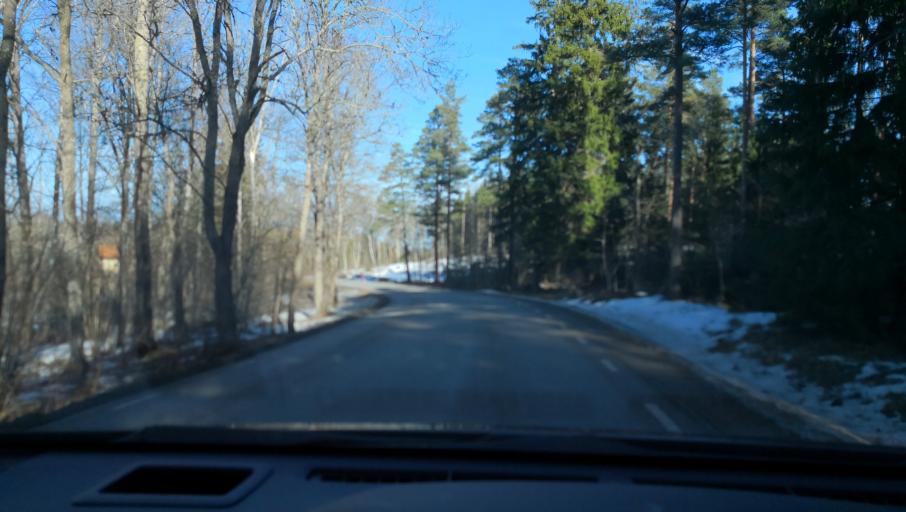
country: SE
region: Uppsala
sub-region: Osthammars Kommun
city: Osterbybruk
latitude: 60.2107
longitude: 17.9042
